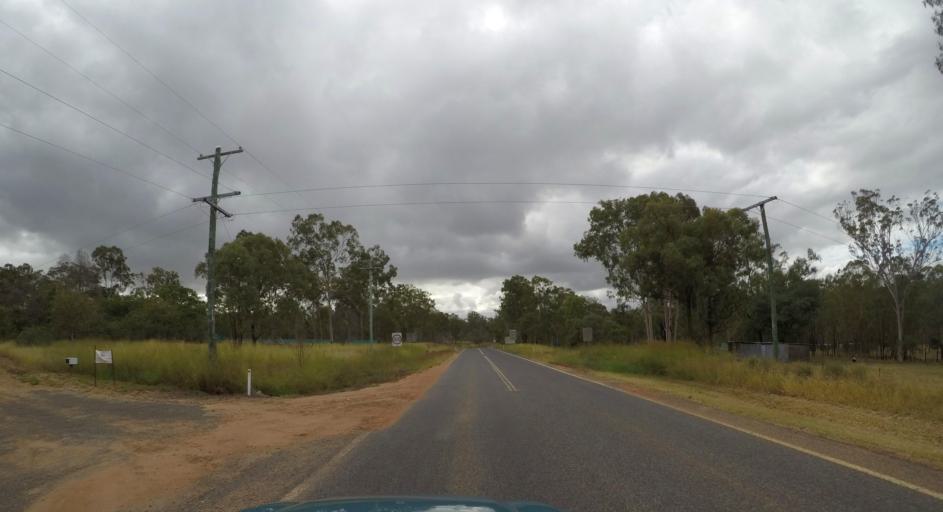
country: AU
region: Queensland
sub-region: North Burnett
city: Gayndah
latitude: -25.3608
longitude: 151.1192
